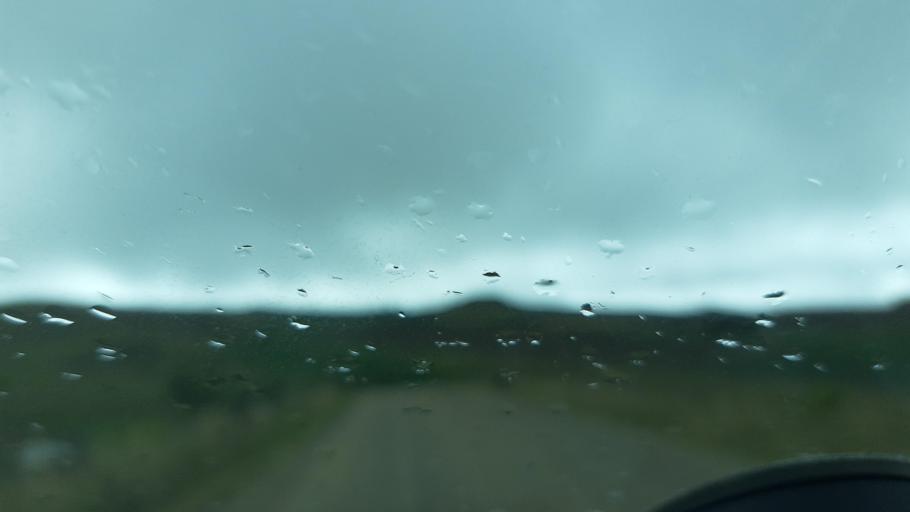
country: CO
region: Boyaca
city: Cucaita
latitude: 5.5184
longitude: -73.4413
